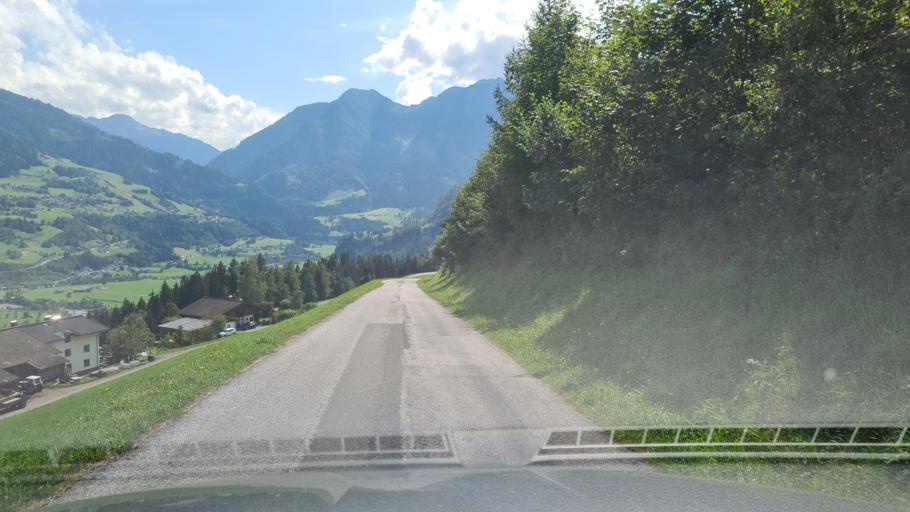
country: AT
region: Salzburg
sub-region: Politischer Bezirk Sankt Johann im Pongau
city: Sankt Johann im Pongau
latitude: 47.3573
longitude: 13.1839
